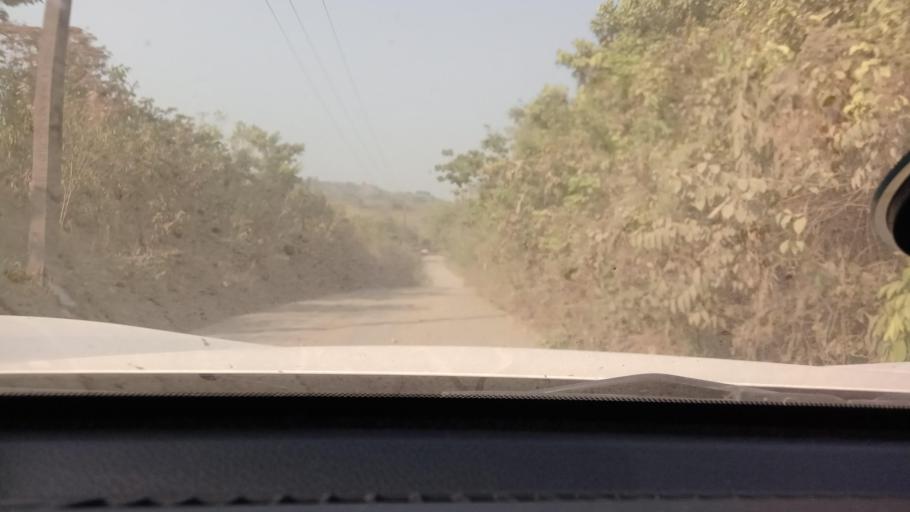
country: MX
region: Tabasco
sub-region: Huimanguillo
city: Francisco Rueda
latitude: 17.6465
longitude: -93.9076
